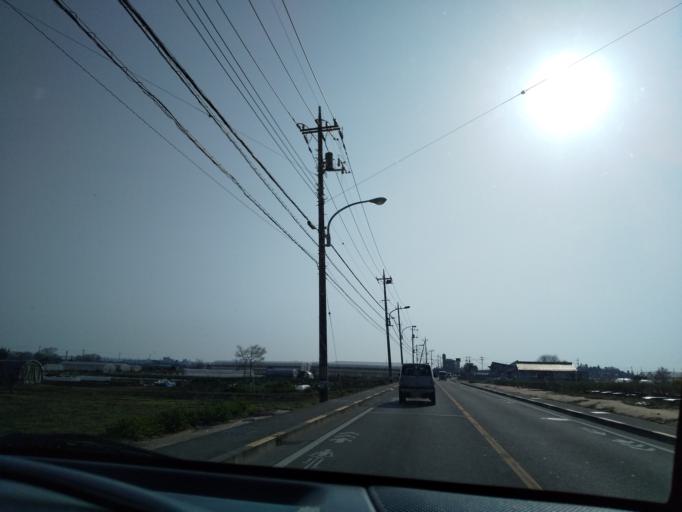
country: JP
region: Tokyo
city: Fussa
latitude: 35.7289
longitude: 139.3038
